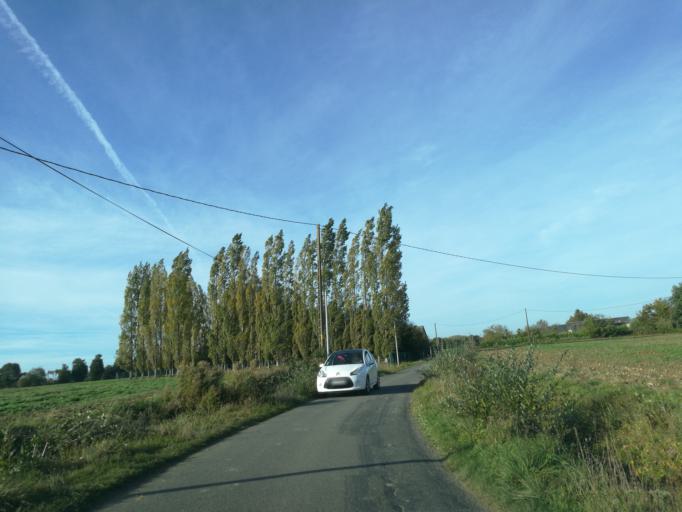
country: FR
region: Brittany
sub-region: Departement d'Ille-et-Vilaine
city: Bedee
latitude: 48.1987
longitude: -1.9548
